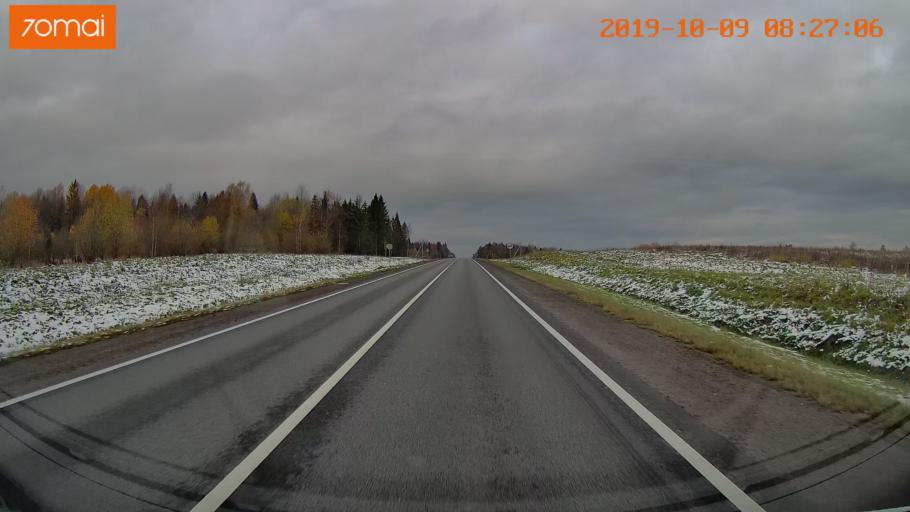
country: RU
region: Vologda
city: Gryazovets
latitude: 58.7996
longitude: 40.2544
